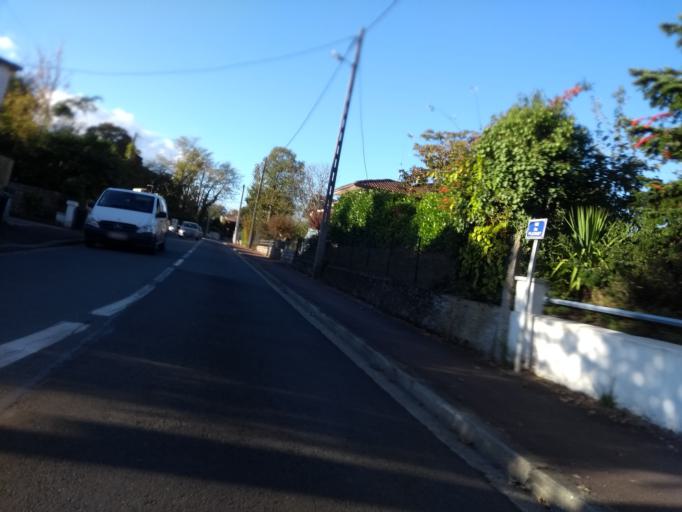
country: FR
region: Aquitaine
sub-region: Departement de la Gironde
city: Gradignan
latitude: 44.7750
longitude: -0.6108
